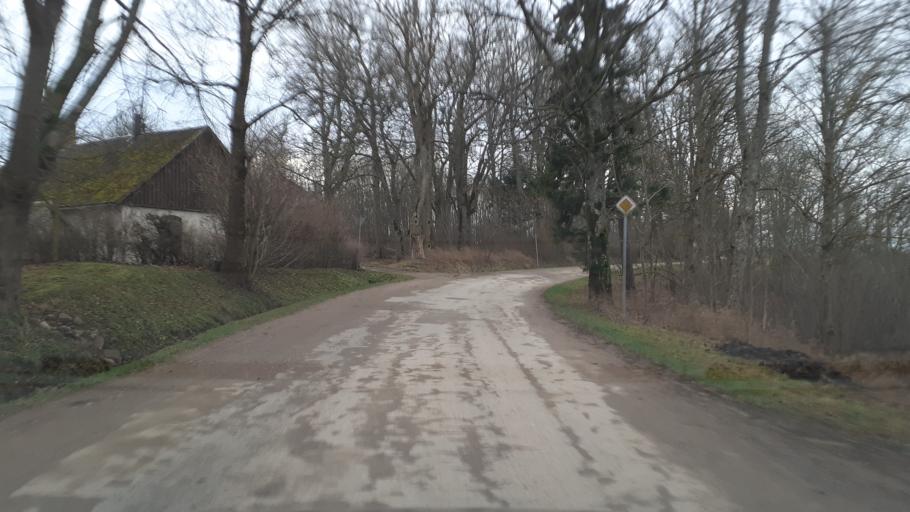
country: LV
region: Aizpute
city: Aizpute
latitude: 56.8022
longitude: 21.6654
